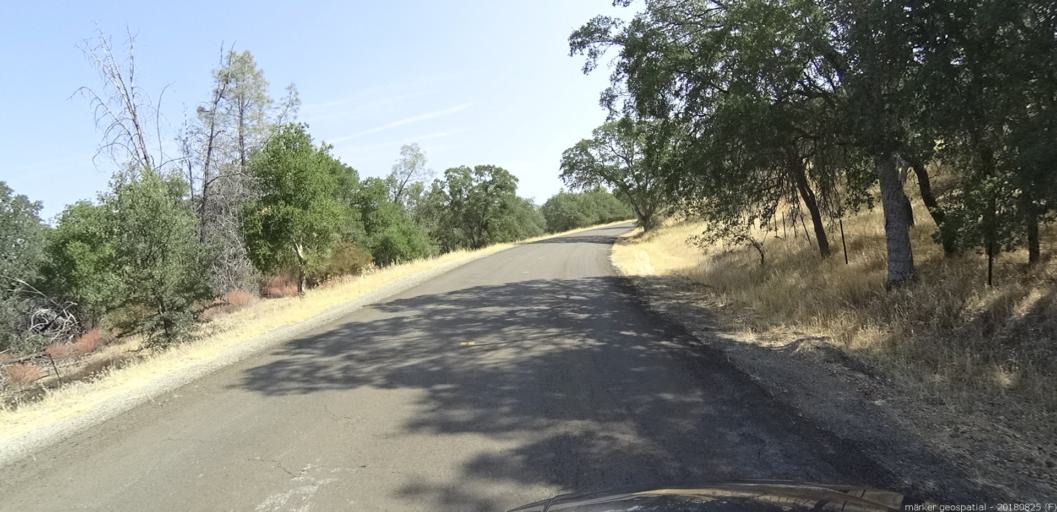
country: US
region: California
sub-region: San Luis Obispo County
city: San Miguel
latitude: 35.9097
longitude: -120.5448
